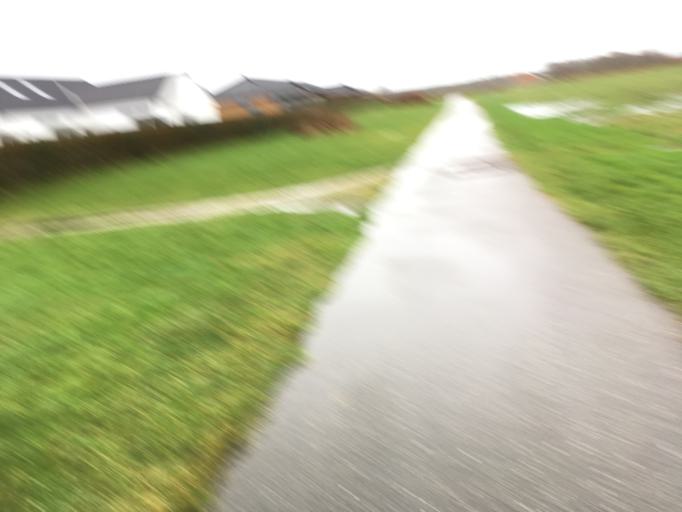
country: DK
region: Central Jutland
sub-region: Ringkobing-Skjern Kommune
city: Ringkobing
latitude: 56.1001
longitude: 8.2674
